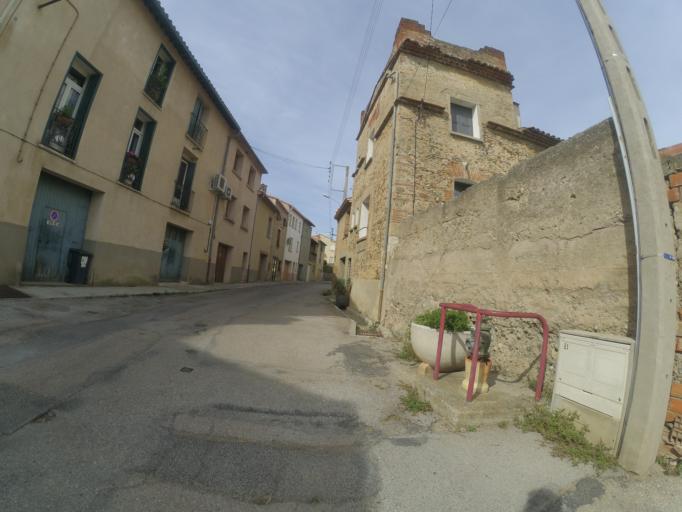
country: FR
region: Languedoc-Roussillon
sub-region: Departement des Pyrenees-Orientales
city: Millas
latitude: 42.6575
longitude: 2.6735
